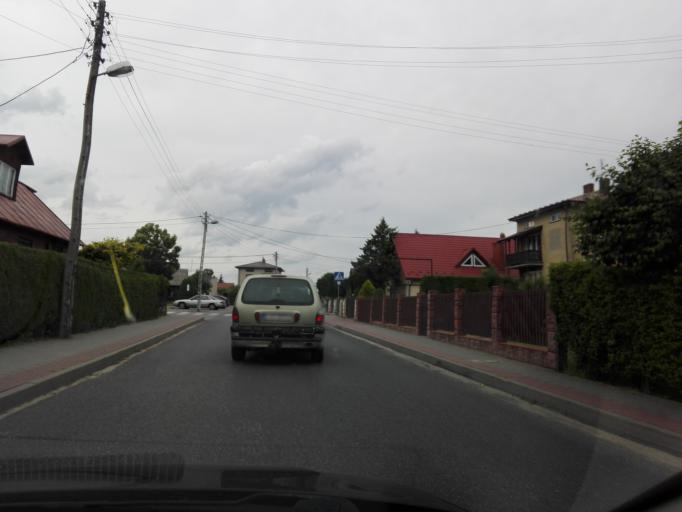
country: PL
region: Lublin Voivodeship
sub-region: Powiat pulawski
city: Kurow
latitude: 51.3899
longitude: 22.1880
